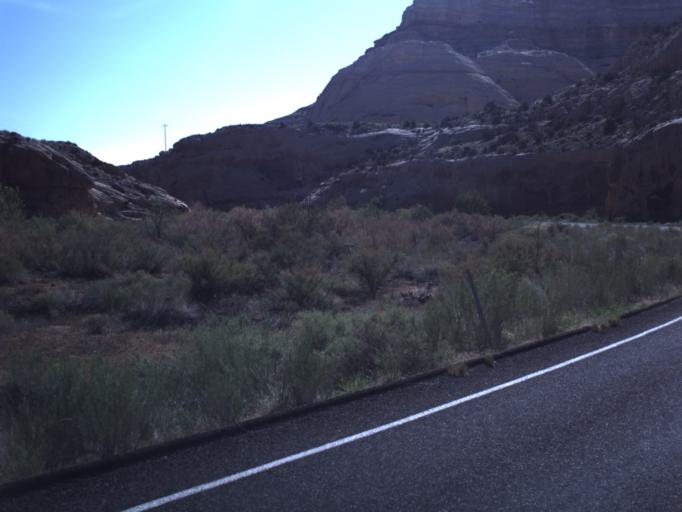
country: US
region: Utah
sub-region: Wayne County
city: Loa
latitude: 38.2815
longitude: -111.1748
